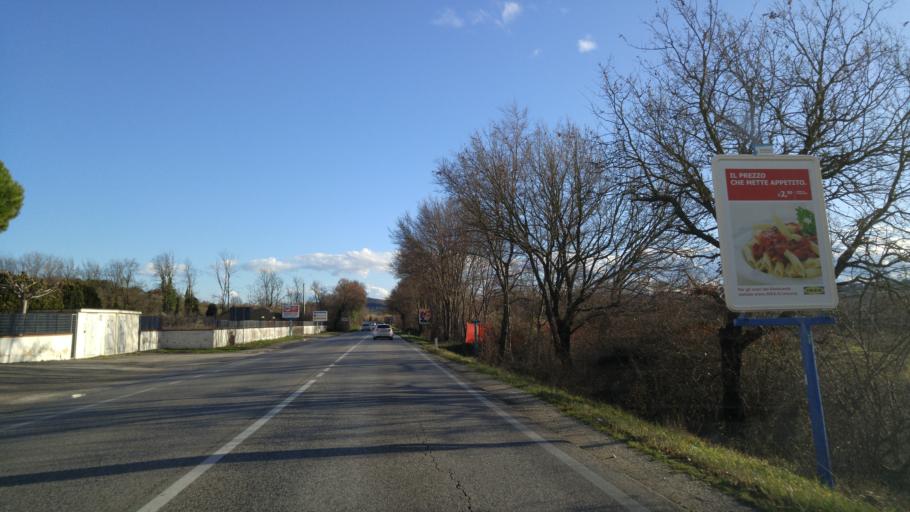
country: IT
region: The Marches
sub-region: Provincia di Ancona
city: Camerano
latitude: 43.5117
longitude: 13.5419
